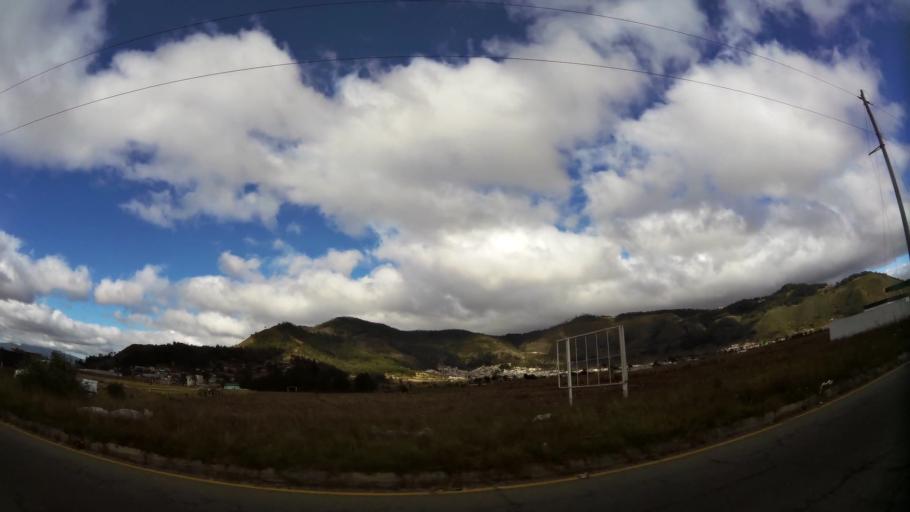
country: GT
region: Quetzaltenango
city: Salcaja
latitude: 14.8880
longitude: -91.4677
